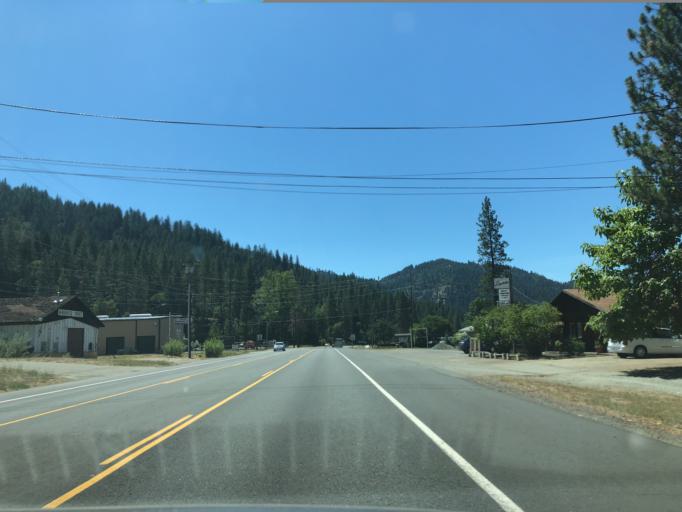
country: US
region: California
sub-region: Trinity County
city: Weaverville
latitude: 40.7145
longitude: -122.9254
